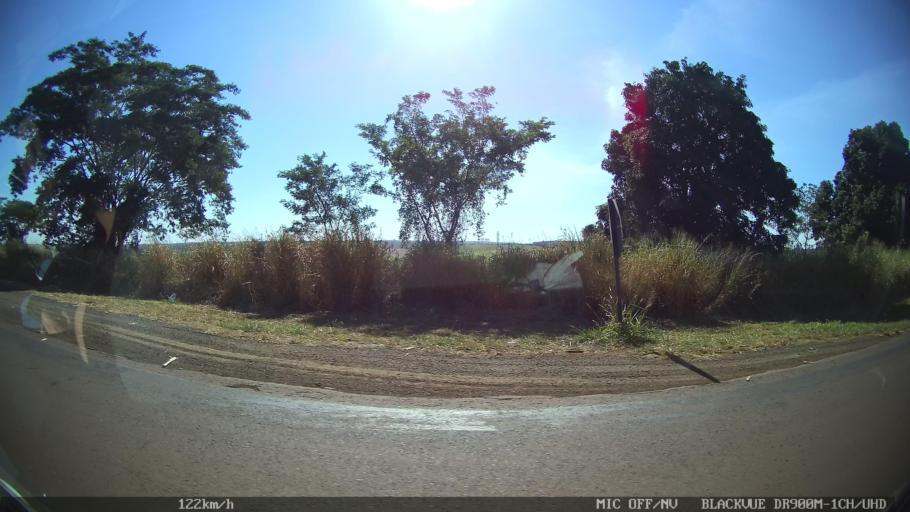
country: BR
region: Sao Paulo
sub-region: Olimpia
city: Olimpia
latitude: -20.6826
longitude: -48.9002
